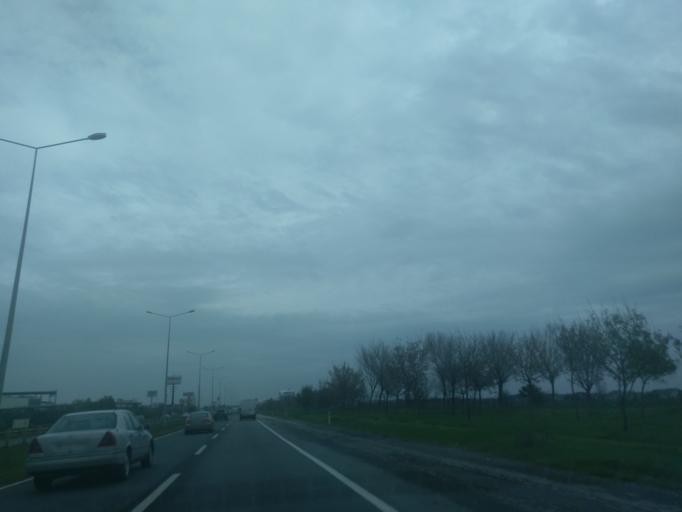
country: TR
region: Istanbul
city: Silivri
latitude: 41.0796
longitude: 28.1982
